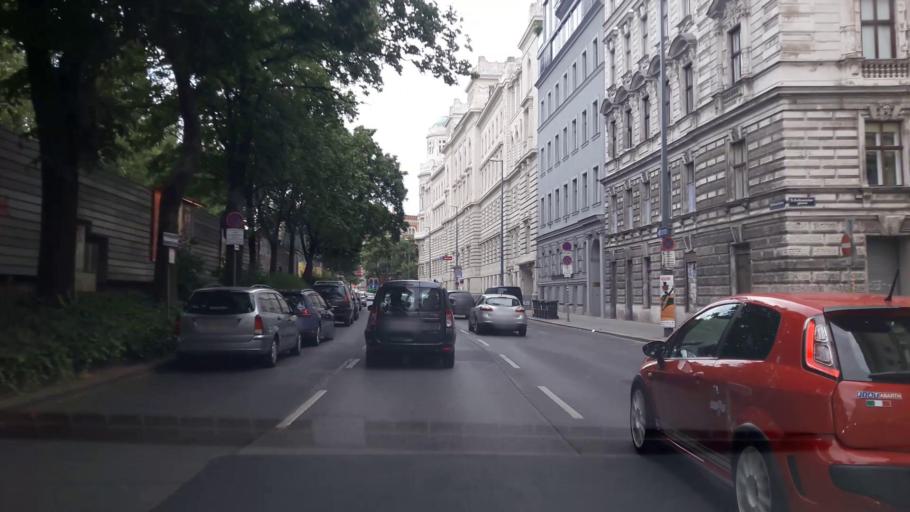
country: AT
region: Vienna
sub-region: Wien Stadt
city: Vienna
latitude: 48.2211
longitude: 16.3674
